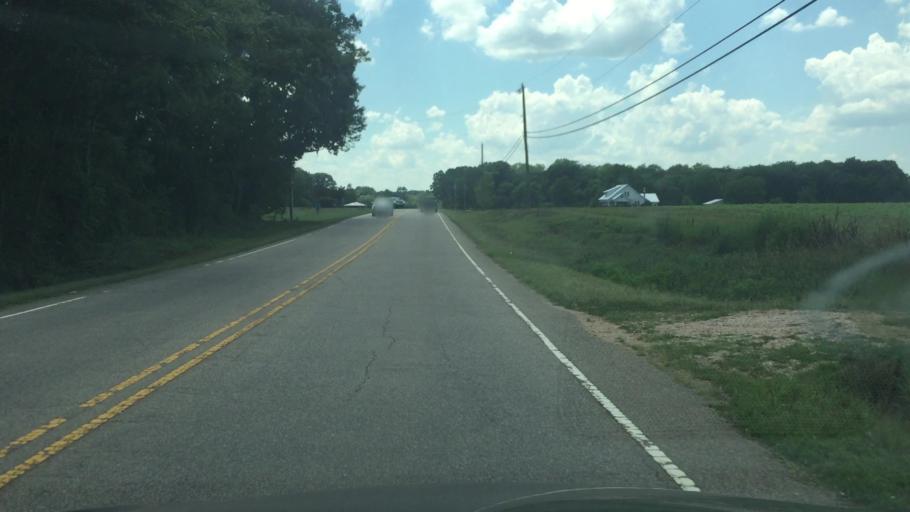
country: US
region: North Carolina
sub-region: Rowan County
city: Enochville
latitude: 35.5772
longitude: -80.7025
